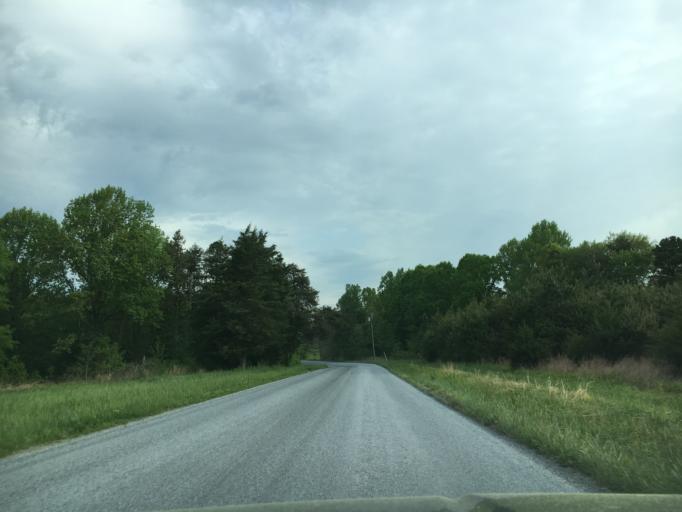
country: US
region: Virginia
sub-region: Campbell County
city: Brookneal
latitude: 36.9499
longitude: -78.9676
